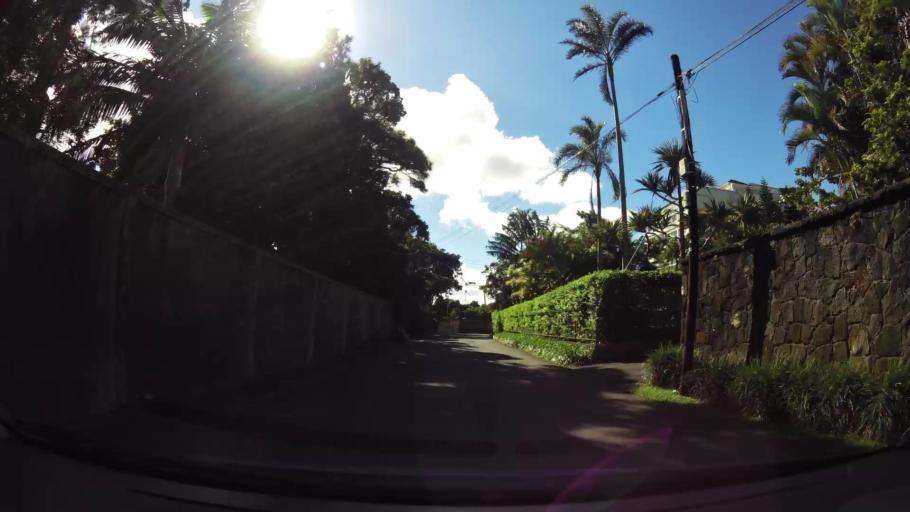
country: MU
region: Plaines Wilhems
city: Curepipe
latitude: -20.3090
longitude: 57.5111
